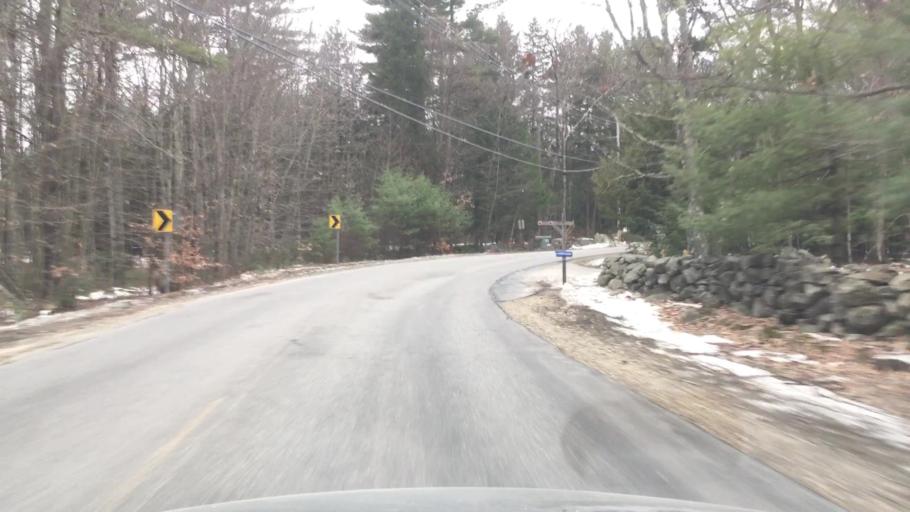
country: US
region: New Hampshire
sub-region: Hillsborough County
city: New Boston
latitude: 42.9724
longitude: -71.6358
